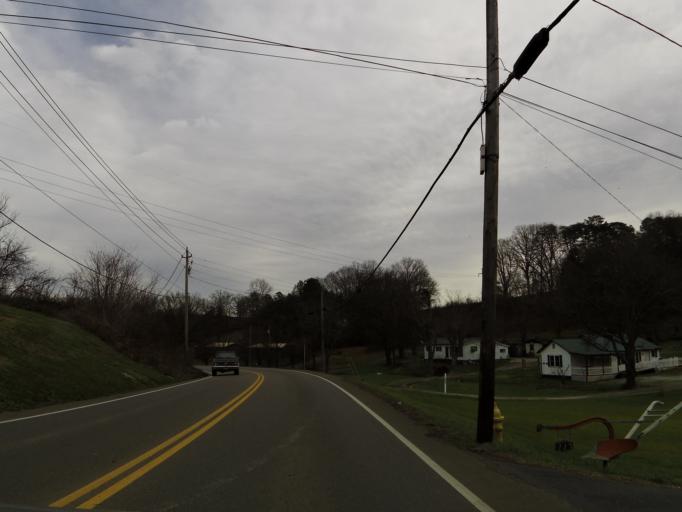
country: US
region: Tennessee
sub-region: Cocke County
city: Newport
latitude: 35.9768
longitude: -83.1714
